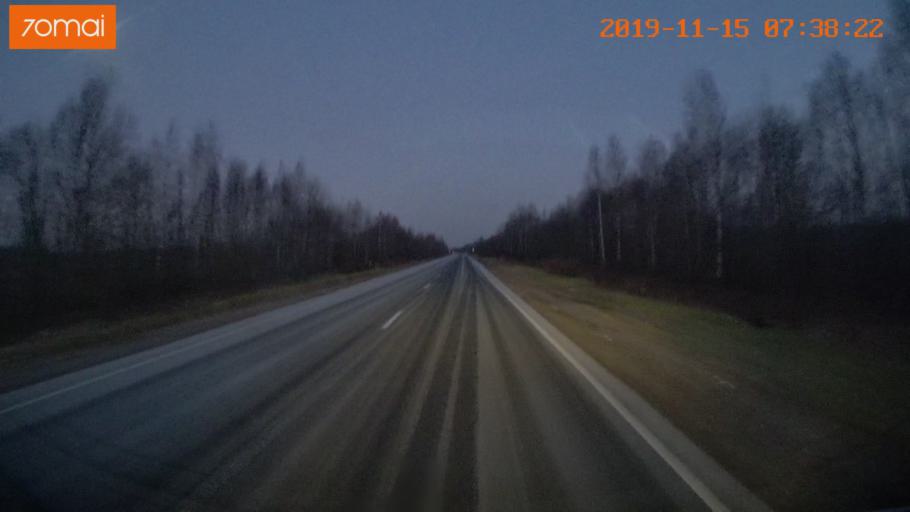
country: RU
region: Vologda
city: Sheksna
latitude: 58.7564
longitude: 38.4030
